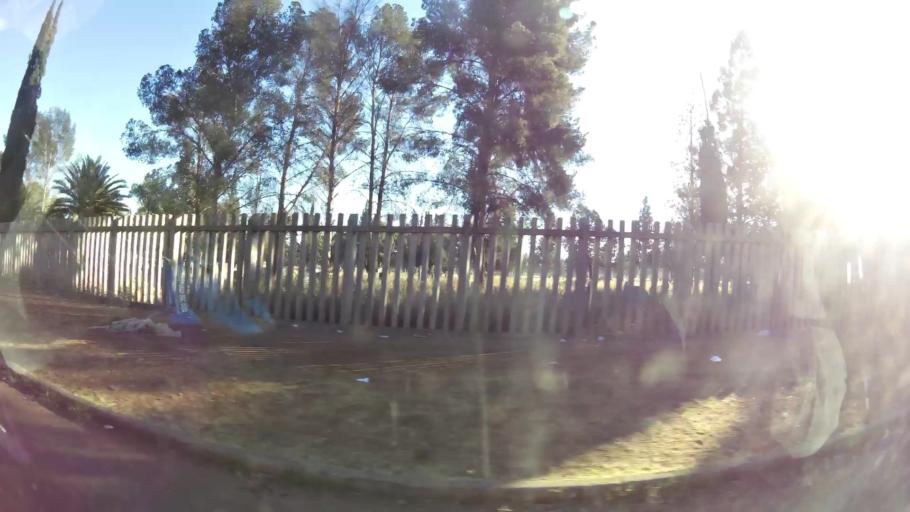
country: ZA
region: Northern Cape
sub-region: Frances Baard District Municipality
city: Kimberley
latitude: -28.7361
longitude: 24.7363
